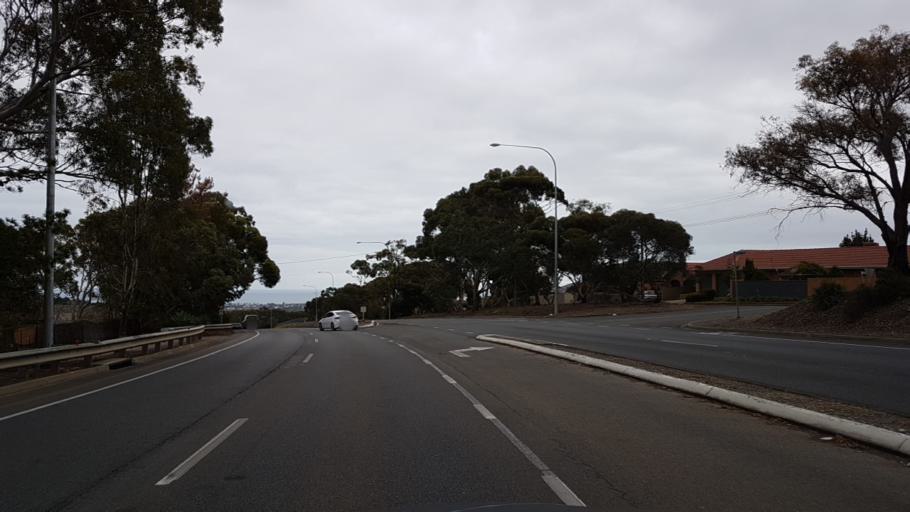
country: AU
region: South Australia
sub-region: Onkaparinga
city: Bedford Park
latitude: -35.0379
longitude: 138.5666
